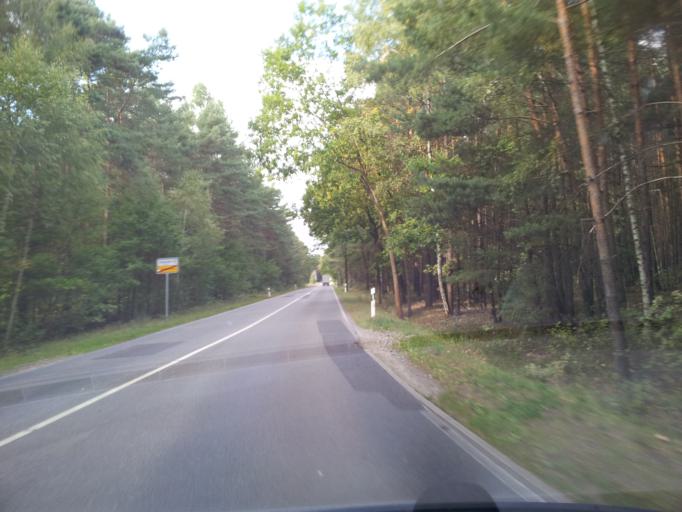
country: DE
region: Brandenburg
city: Sallgast
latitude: 51.6021
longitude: 13.7767
